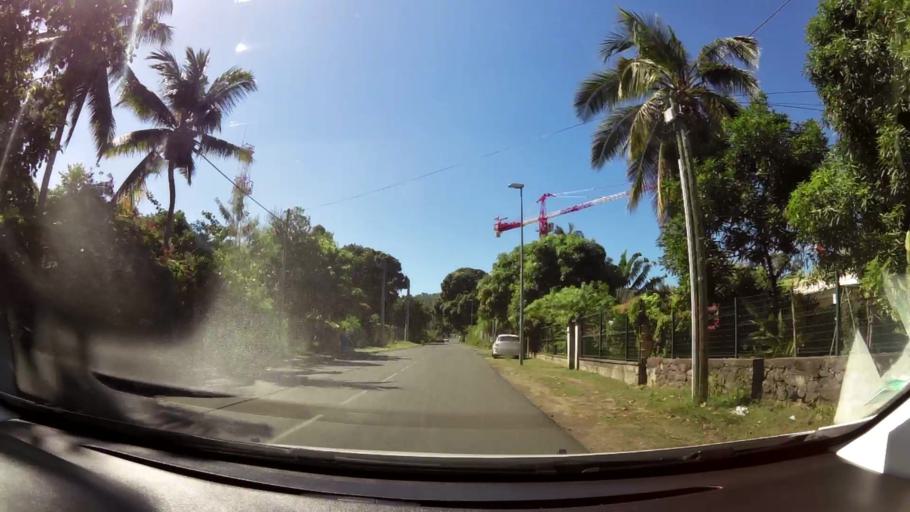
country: YT
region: Pamandzi
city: Pamandzi
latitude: -12.7956
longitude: 45.2761
